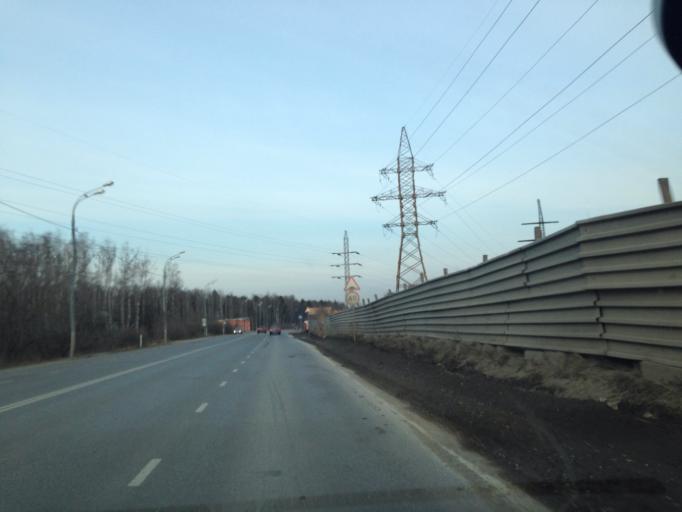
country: RU
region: Moscow
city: Vostochnyy
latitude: 55.8036
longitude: 37.9054
